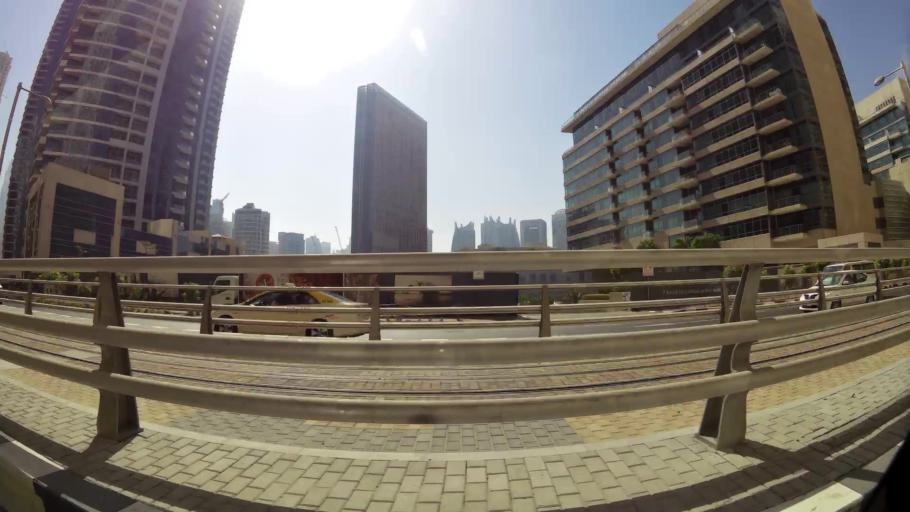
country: AE
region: Dubai
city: Dubai
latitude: 25.0780
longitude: 55.1365
